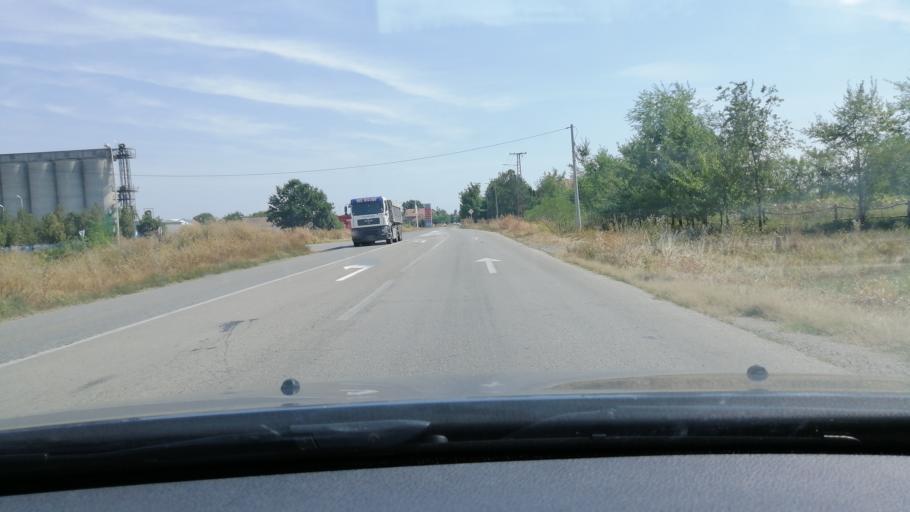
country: RS
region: Autonomna Pokrajina Vojvodina
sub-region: Srednjebanatski Okrug
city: Secanj
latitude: 45.3694
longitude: 20.7584
